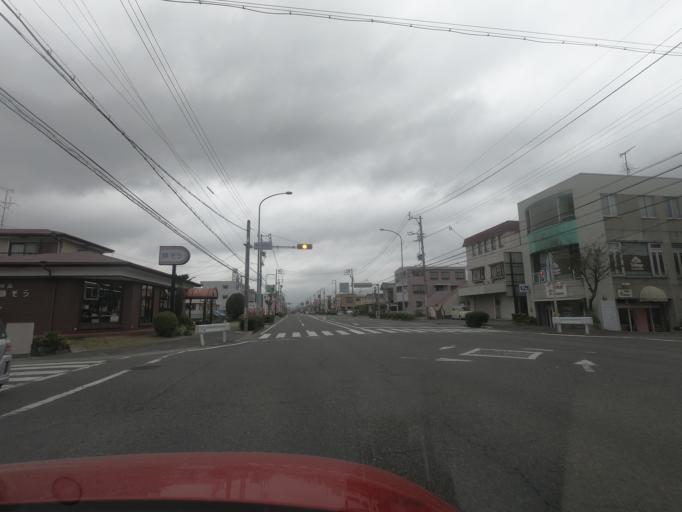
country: JP
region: Aichi
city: Kasugai
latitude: 35.2551
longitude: 136.9696
